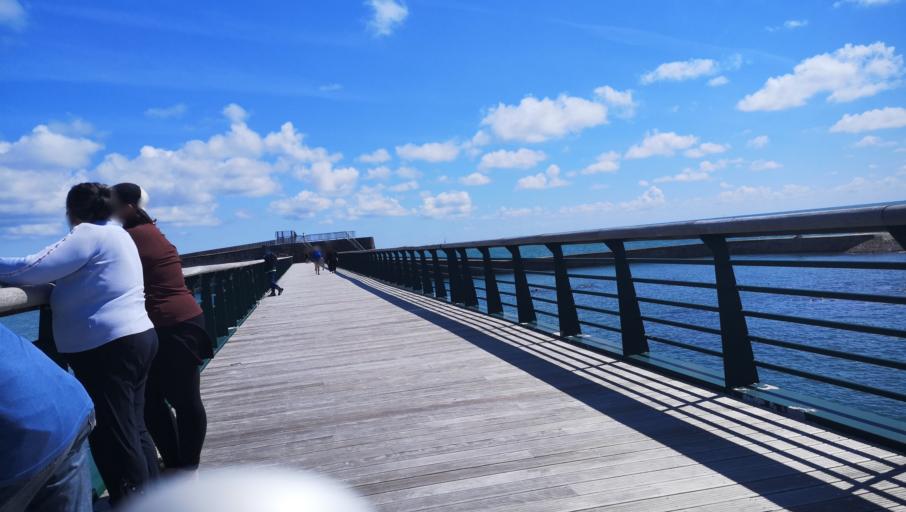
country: FR
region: Pays de la Loire
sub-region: Departement de la Vendee
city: Les Sables-d'Olonne
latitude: 46.4890
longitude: -1.7931
